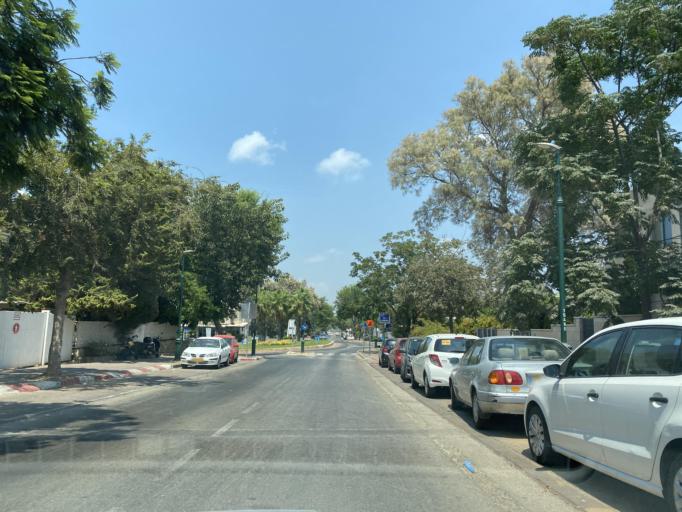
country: IL
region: Tel Aviv
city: Herzliya Pituah
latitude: 32.1784
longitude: 34.8056
